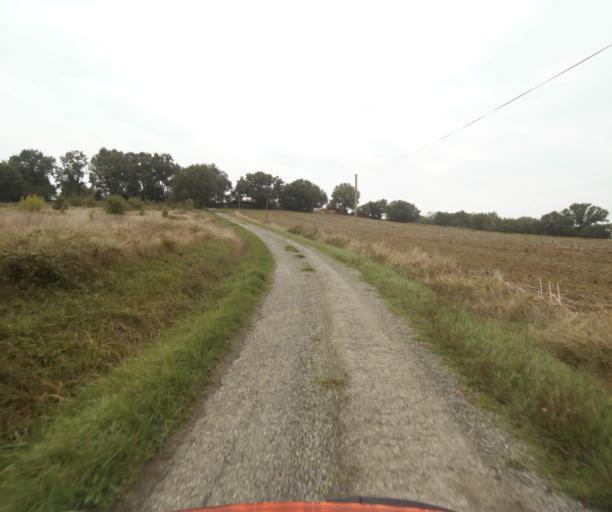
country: FR
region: Midi-Pyrenees
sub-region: Departement de la Haute-Garonne
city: Launac
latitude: 43.7960
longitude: 1.2104
